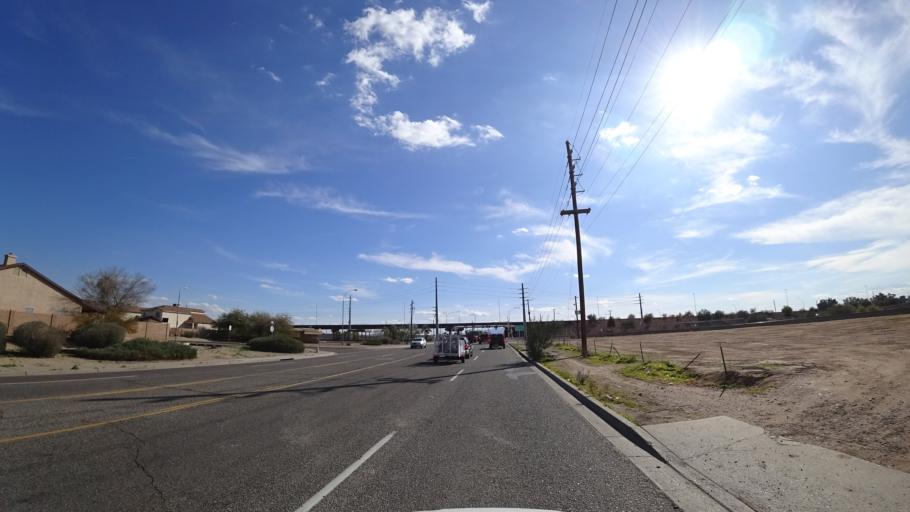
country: US
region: Arizona
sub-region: Maricopa County
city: Peoria
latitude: 33.5687
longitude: -112.2204
